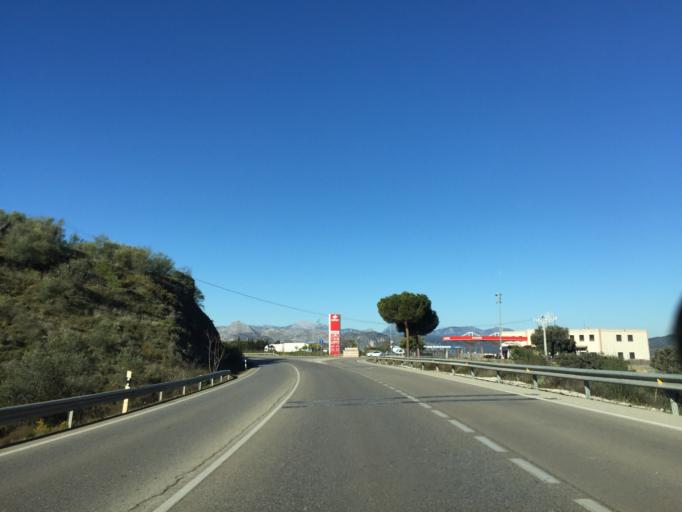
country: ES
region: Andalusia
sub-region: Provincia de Malaga
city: Ronda
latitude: 36.7592
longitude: -5.1606
